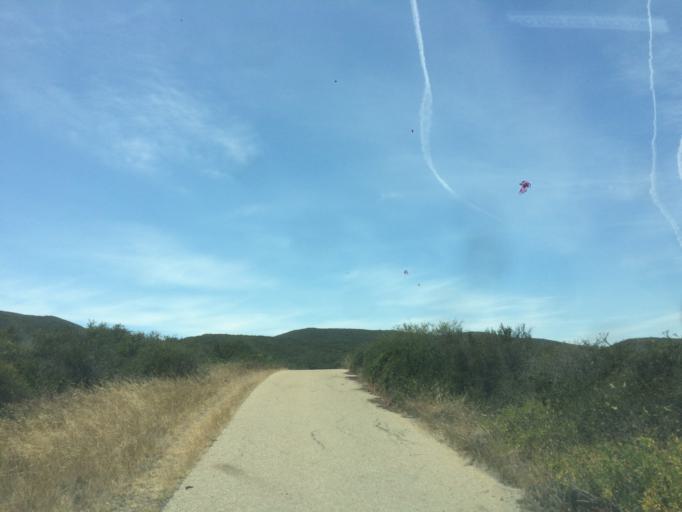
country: US
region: California
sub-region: San Luis Obispo County
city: San Luis Obispo
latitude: 35.2529
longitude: -120.7050
